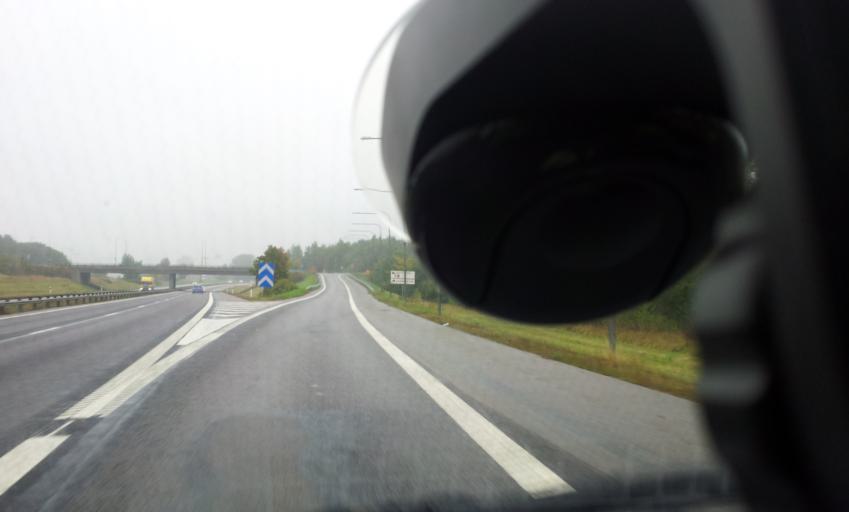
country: SE
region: OEstergoetland
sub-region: Norrkopings Kommun
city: Norrkoping
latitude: 58.5639
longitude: 16.2225
